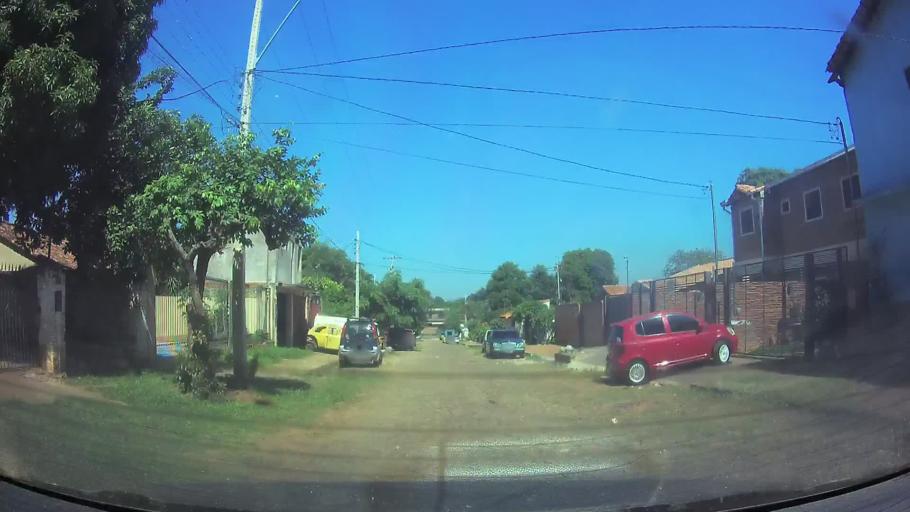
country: PY
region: Central
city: Fernando de la Mora
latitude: -25.3040
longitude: -57.5297
